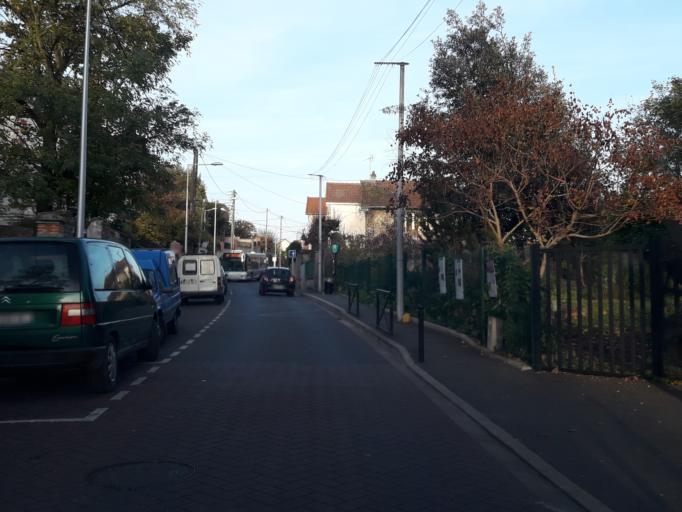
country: FR
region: Ile-de-France
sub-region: Departement de l'Essonne
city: Vigneux-sur-Seine
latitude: 48.7149
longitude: 2.4046
